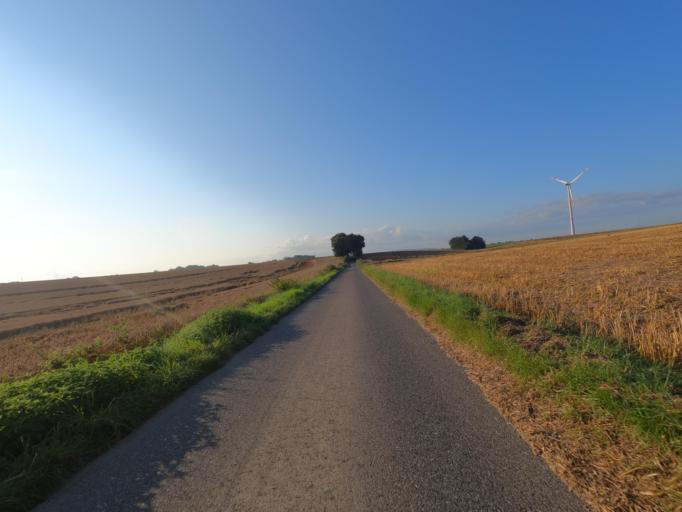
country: DE
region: North Rhine-Westphalia
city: Erkelenz
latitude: 51.0223
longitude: 6.3540
